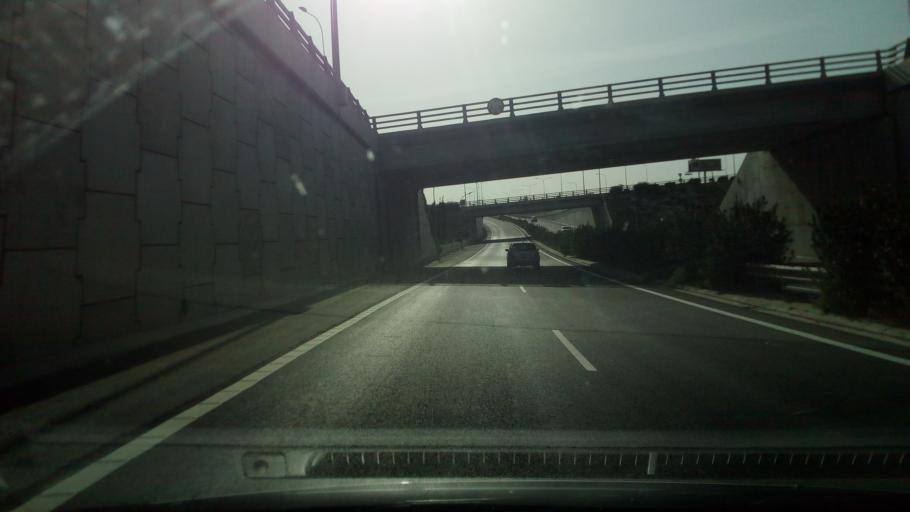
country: CY
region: Larnaka
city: Aradippou
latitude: 34.9530
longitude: 33.5742
